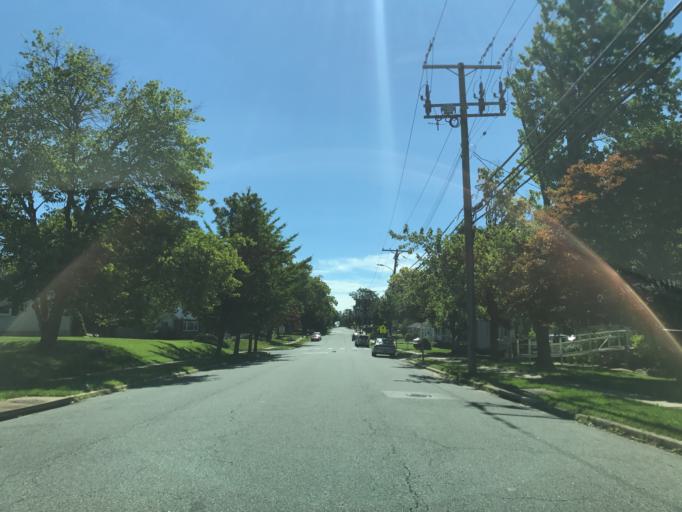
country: US
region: Maryland
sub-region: Howard County
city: Ellicott City
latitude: 39.2800
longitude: -76.7730
